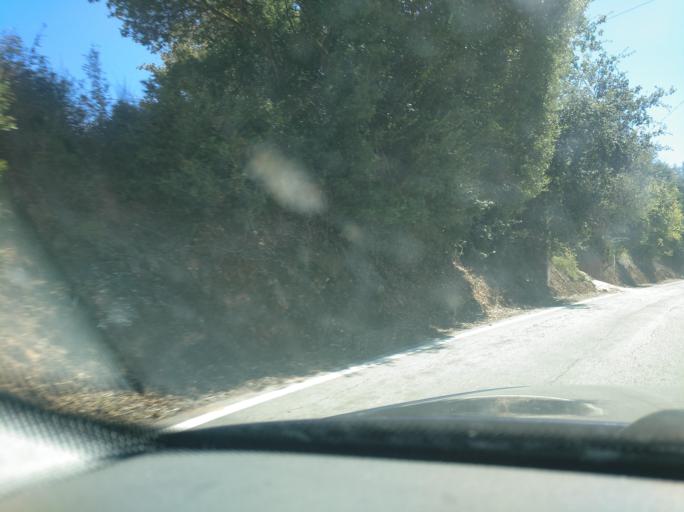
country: PT
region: Leiria
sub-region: Alcobaca
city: Aljubarrota
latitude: 39.5687
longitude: -8.9337
